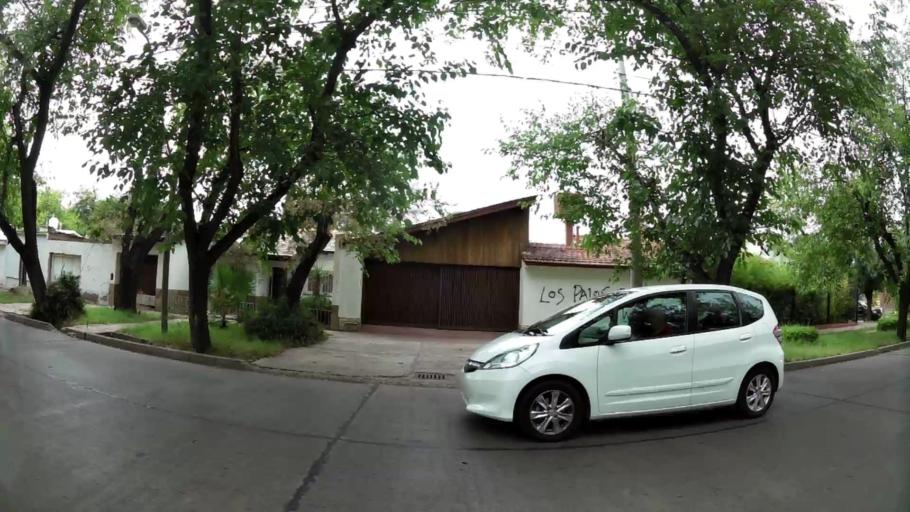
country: AR
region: Mendoza
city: Las Heras
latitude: -32.8719
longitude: -68.8551
